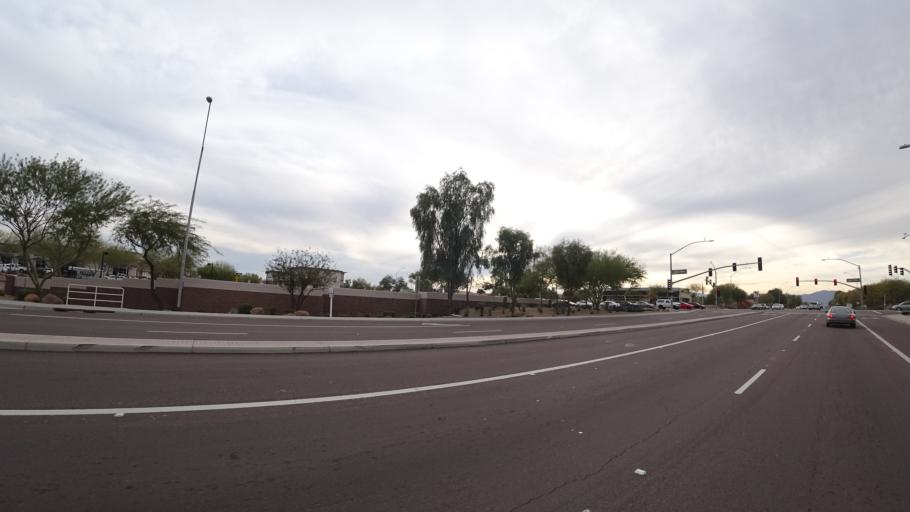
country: US
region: Arizona
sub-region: Maricopa County
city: Surprise
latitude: 33.6241
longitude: -112.3931
